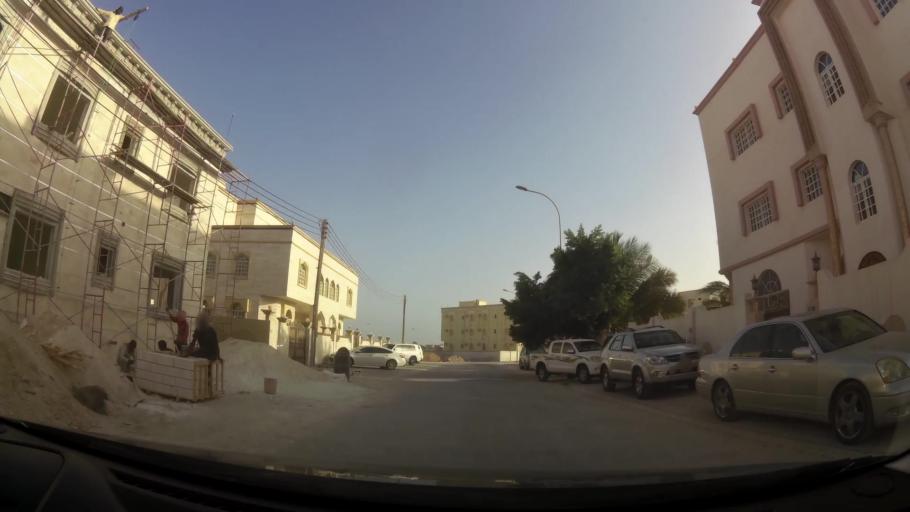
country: OM
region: Zufar
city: Salalah
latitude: 17.0124
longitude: 54.0338
